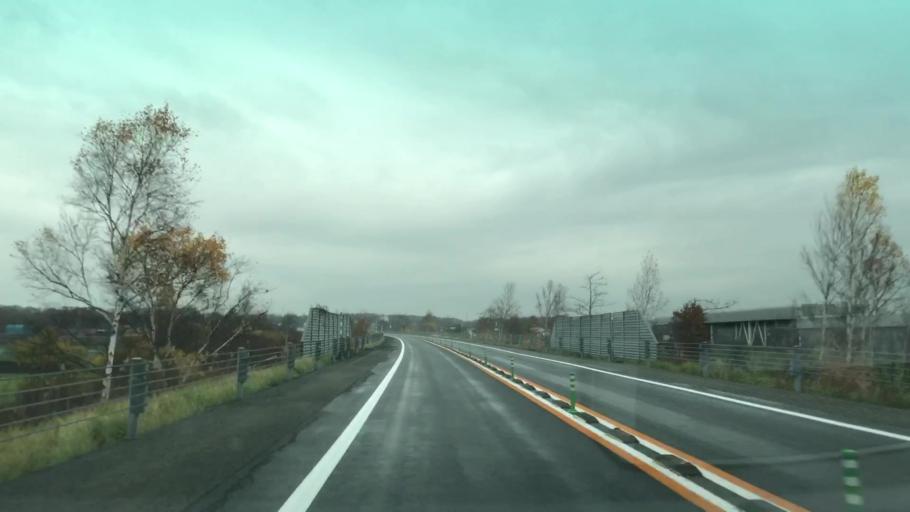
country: JP
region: Hokkaido
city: Chitose
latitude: 42.8636
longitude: 141.6083
